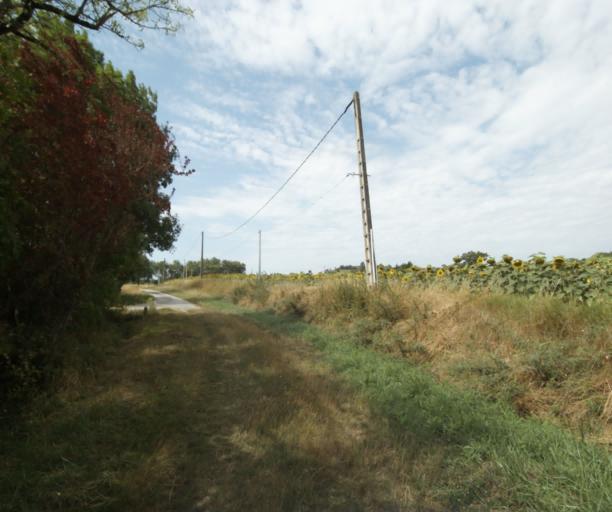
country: FR
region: Midi-Pyrenees
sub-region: Departement de la Haute-Garonne
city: Saint-Felix-Lauragais
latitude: 43.4511
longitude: 1.9126
